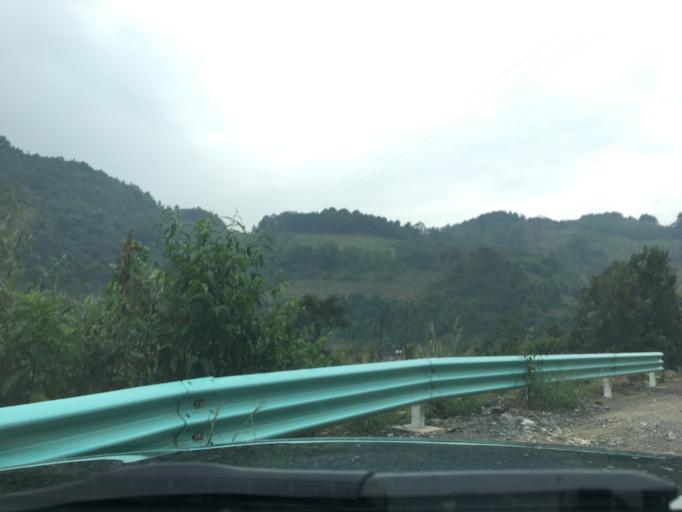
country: CN
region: Guangxi Zhuangzu Zizhiqu
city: Xinzhou
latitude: 25.0490
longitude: 105.9152
